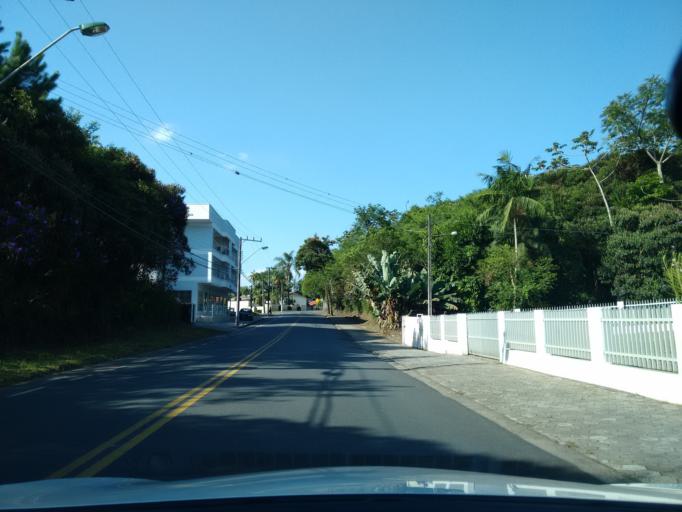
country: BR
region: Santa Catarina
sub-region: Blumenau
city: Blumenau
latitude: -26.8986
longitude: -49.0656
